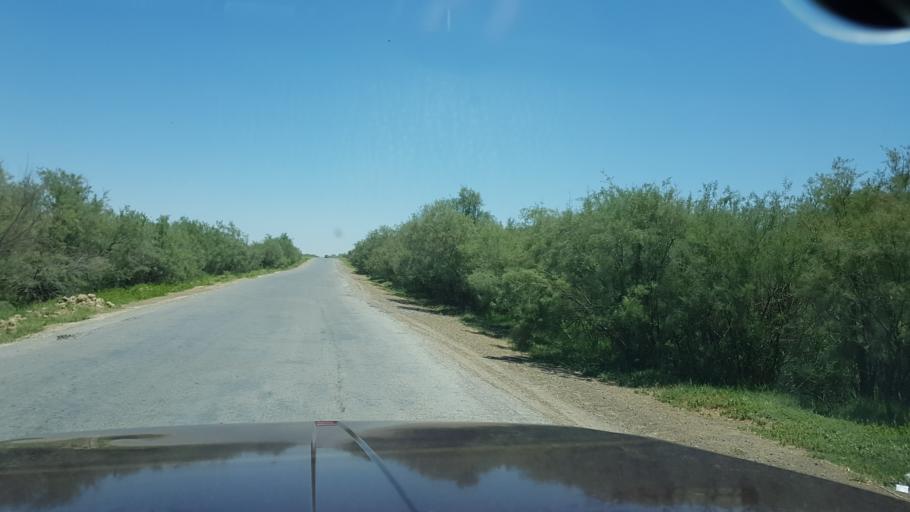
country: TM
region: Ahal
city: Annau
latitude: 37.8849
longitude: 58.7363
